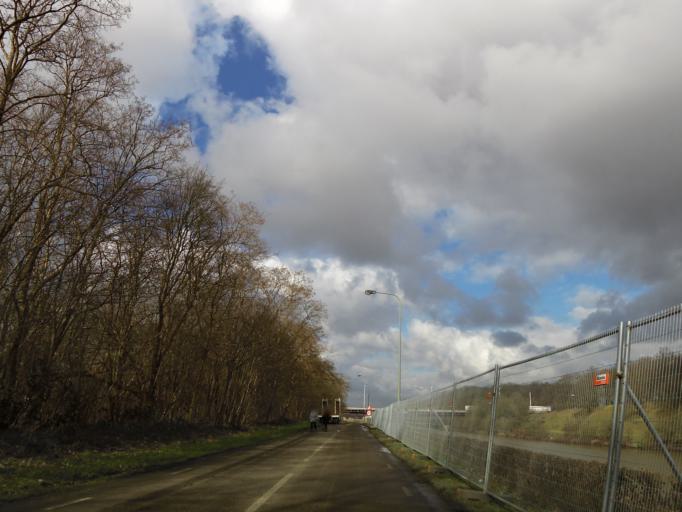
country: NL
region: Limburg
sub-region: Gemeente Stein
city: Elsloo
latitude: 50.9567
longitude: 5.7591
